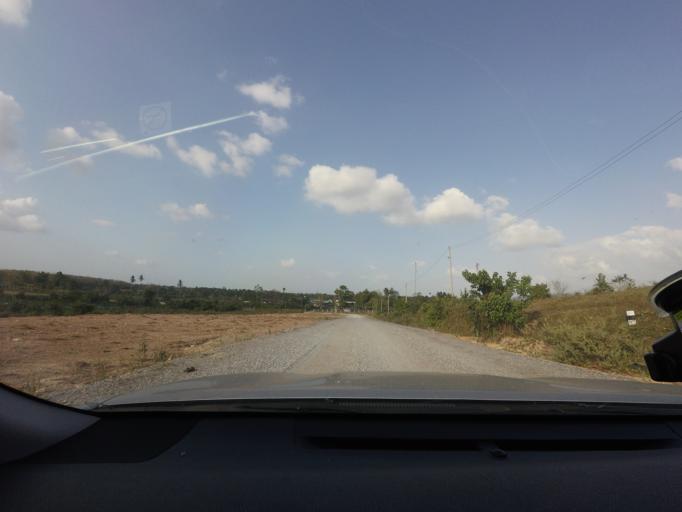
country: TH
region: Pattani
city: Mae Lan
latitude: 6.6130
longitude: 101.2568
